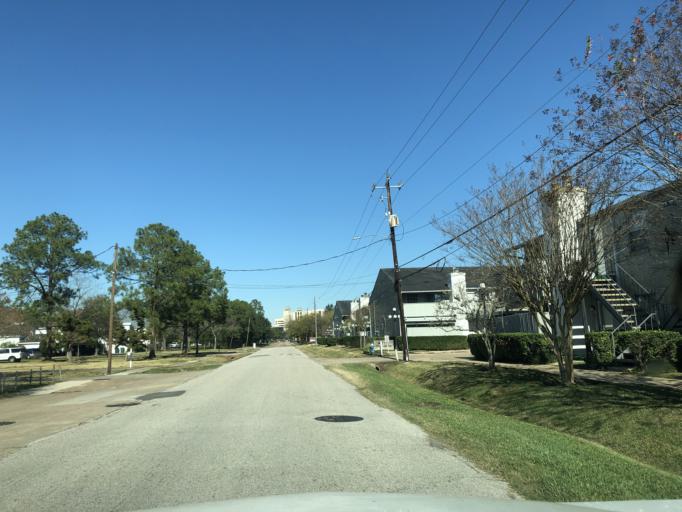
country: US
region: Texas
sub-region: Harris County
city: Bellaire
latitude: 29.6840
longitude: -95.5218
